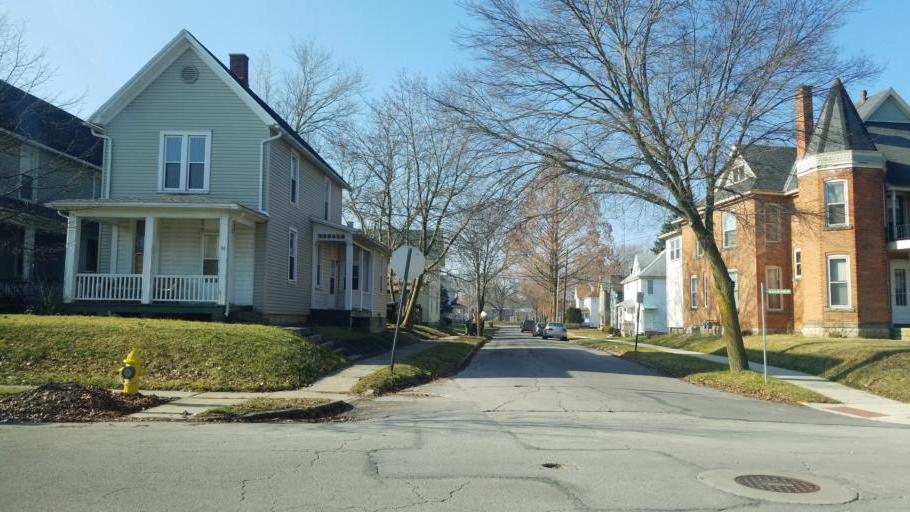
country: US
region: Ohio
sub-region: Seneca County
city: Tiffin
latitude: 41.1131
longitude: -83.1696
